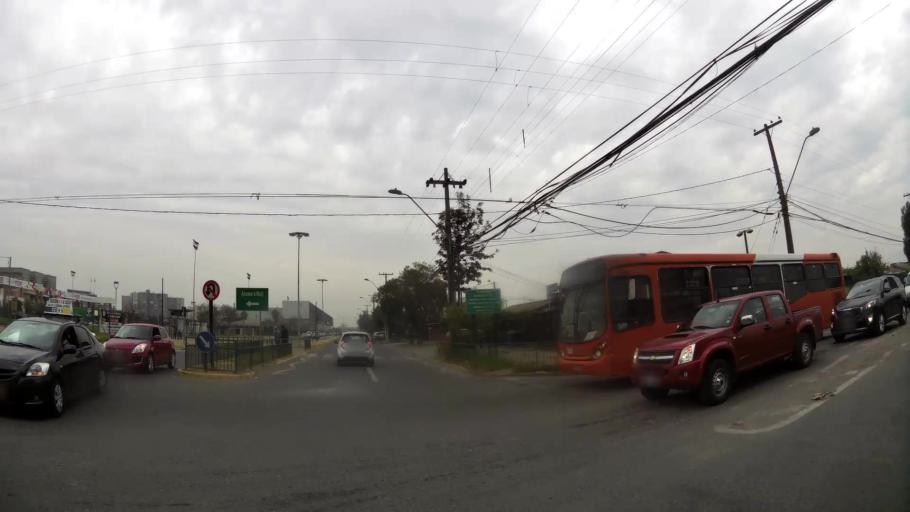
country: CL
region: Santiago Metropolitan
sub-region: Provincia de Santiago
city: Villa Presidente Frei, Nunoa, Santiago, Chile
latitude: -33.5140
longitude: -70.5942
